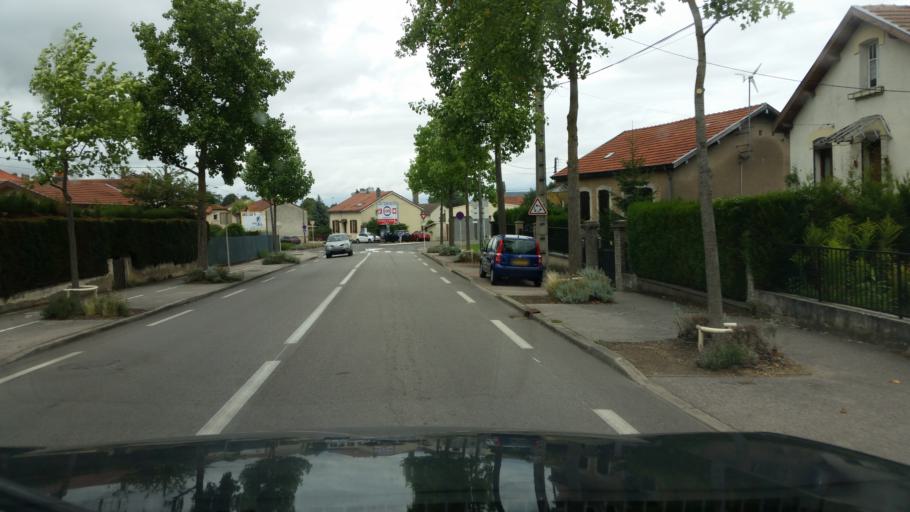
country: FR
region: Lorraine
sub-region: Departement de Meurthe-et-Moselle
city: Toul
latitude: 48.6658
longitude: 5.8816
